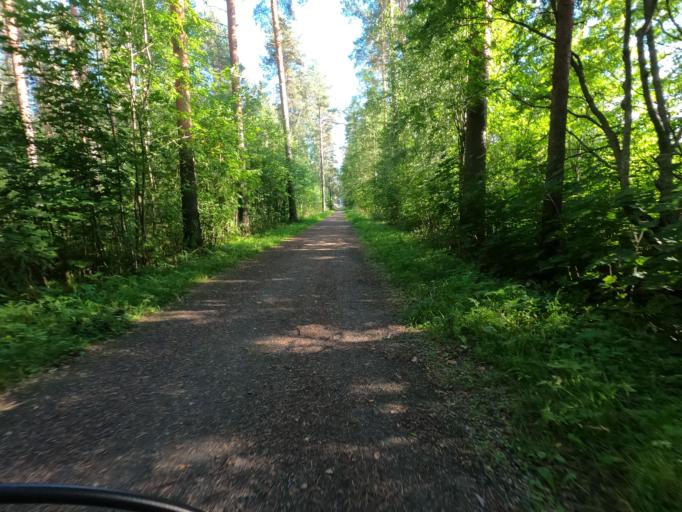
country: FI
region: North Karelia
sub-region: Joensuu
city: Joensuu
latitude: 62.6136
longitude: 29.7583
